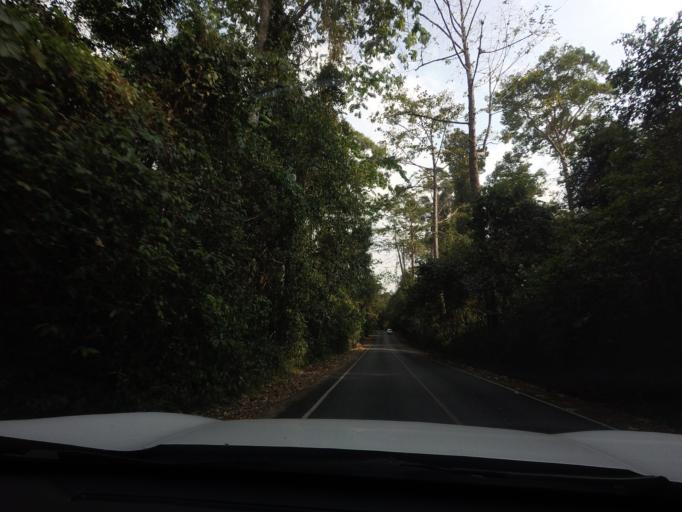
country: TH
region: Nakhon Ratchasima
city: Pak Chong
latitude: 14.4365
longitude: 101.4092
